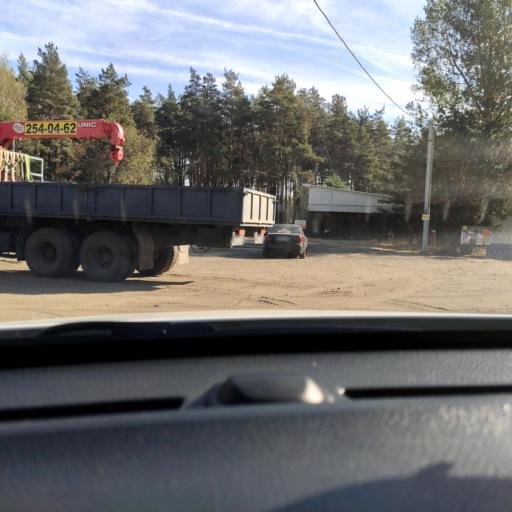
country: RU
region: Voronezj
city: Pridonskoy
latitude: 51.6897
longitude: 39.1037
